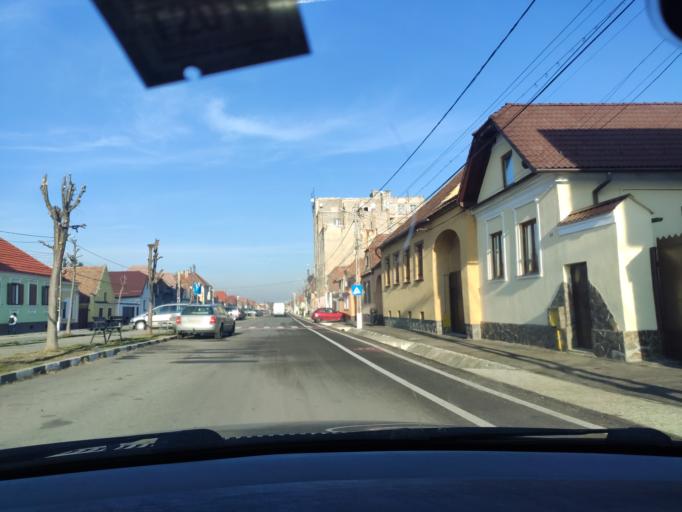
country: RO
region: Brasov
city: Codlea
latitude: 45.6985
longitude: 25.4495
